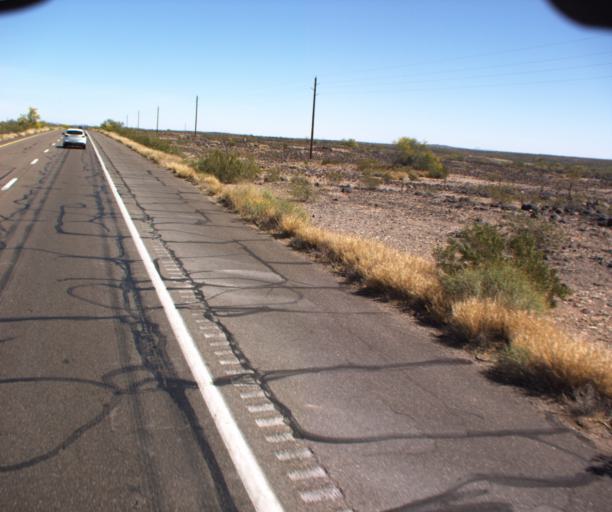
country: US
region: Arizona
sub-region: Maricopa County
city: Gila Bend
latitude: 32.8527
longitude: -113.2567
